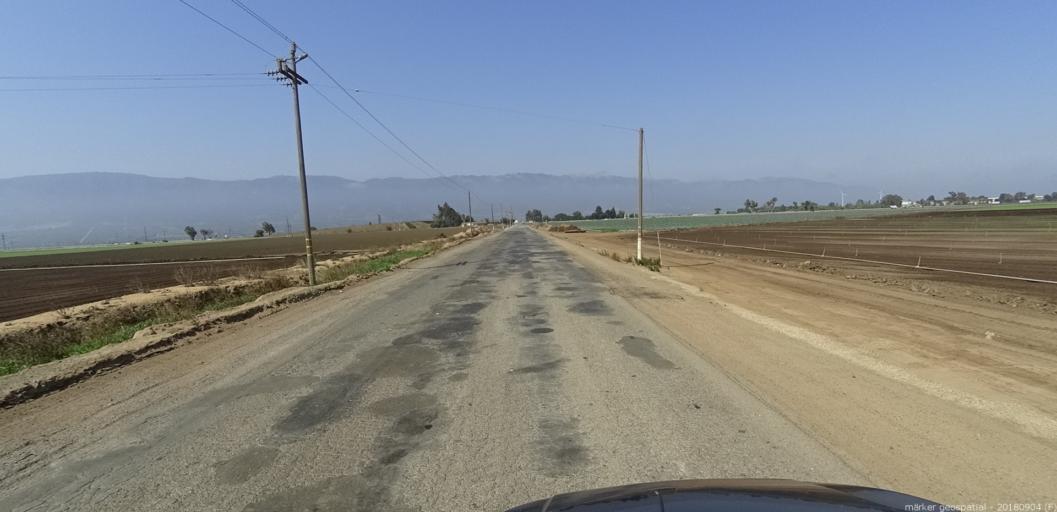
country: US
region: California
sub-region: Monterey County
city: Gonzales
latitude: 36.4958
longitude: -121.4206
